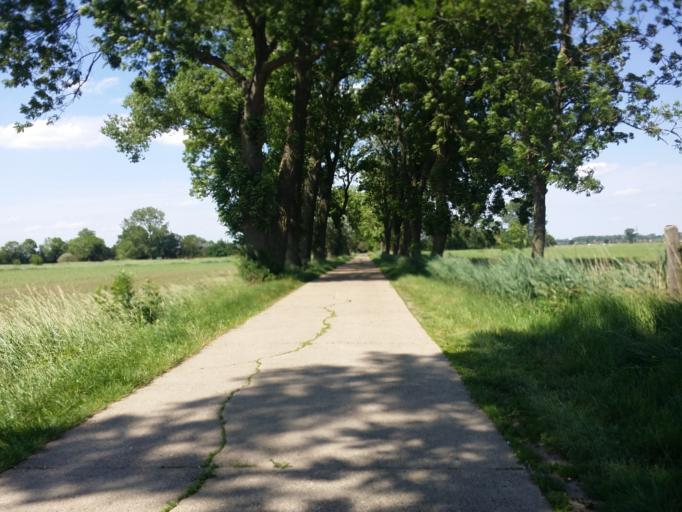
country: DE
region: Lower Saxony
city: Neuenkirchen
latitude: 53.1700
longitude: 8.5082
